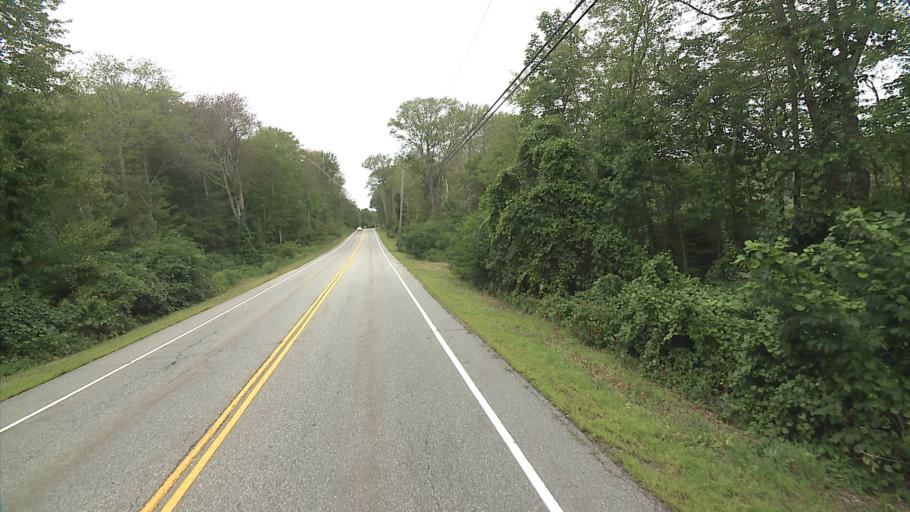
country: US
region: Connecticut
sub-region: Hartford County
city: Terramuggus
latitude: 41.7141
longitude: -72.4333
